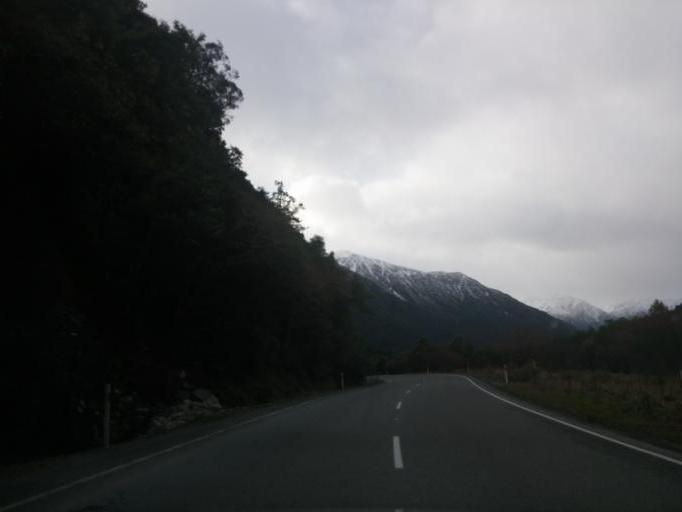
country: NZ
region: West Coast
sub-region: Grey District
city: Greymouth
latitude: -42.8206
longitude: 171.5629
